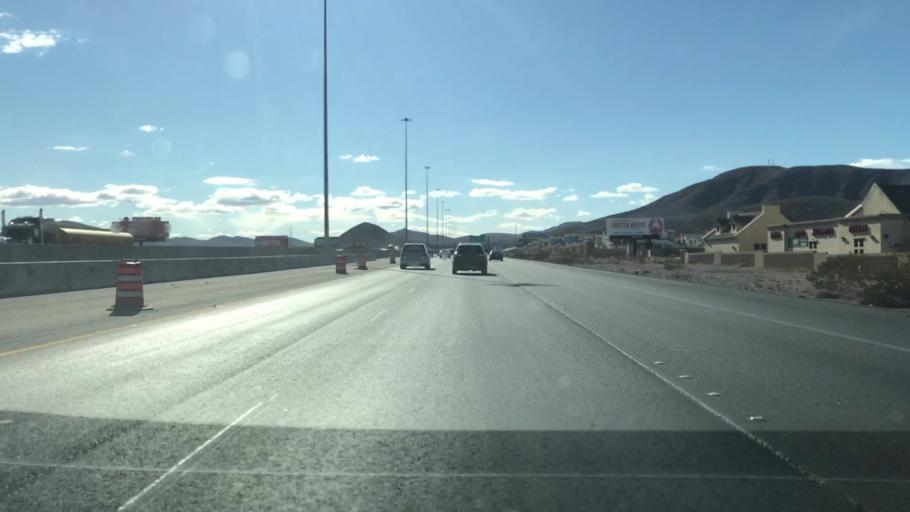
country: US
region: Nevada
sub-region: Clark County
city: Enterprise
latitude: 35.9739
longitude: -115.1815
